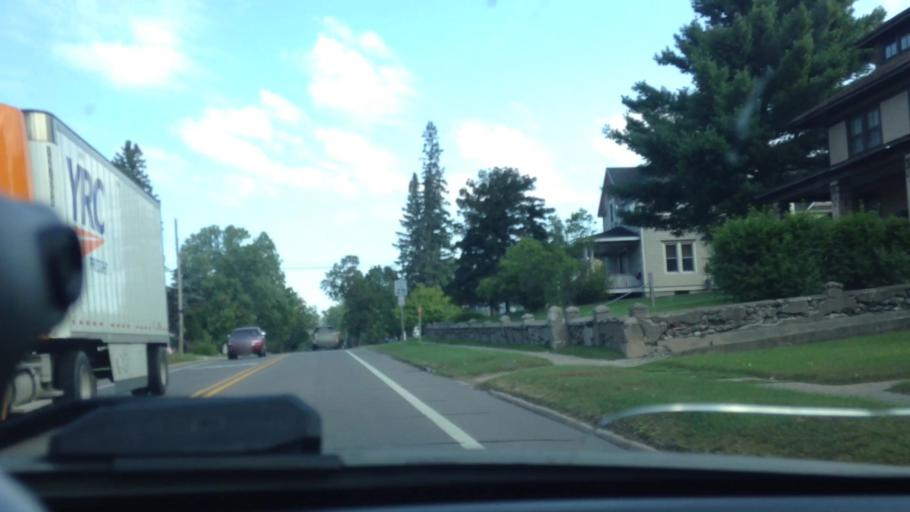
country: US
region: Michigan
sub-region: Dickinson County
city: Norway
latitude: 45.7830
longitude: -87.9098
